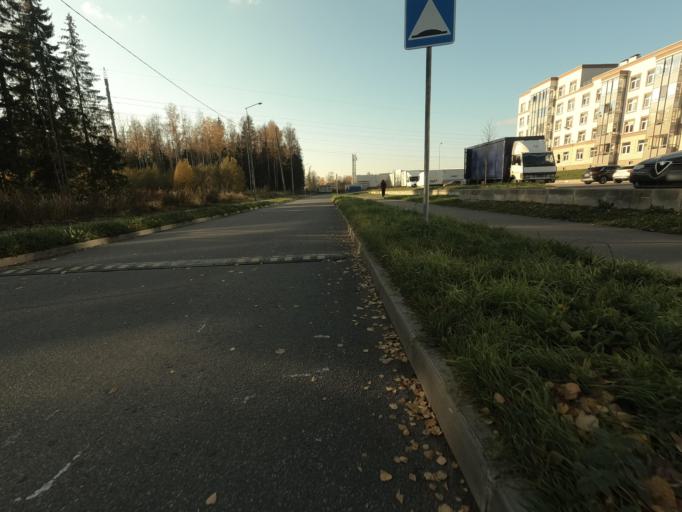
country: RU
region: Leningrad
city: Sertolovo
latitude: 60.1641
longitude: 30.1884
